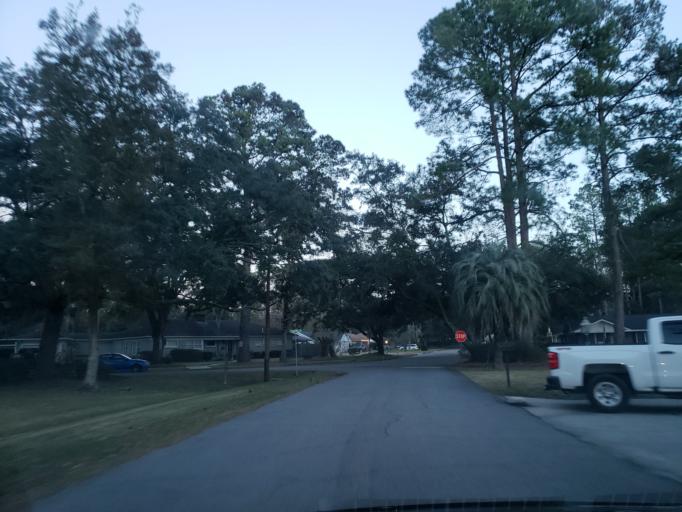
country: US
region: Georgia
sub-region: Chatham County
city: Thunderbolt
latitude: 32.0183
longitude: -81.0840
